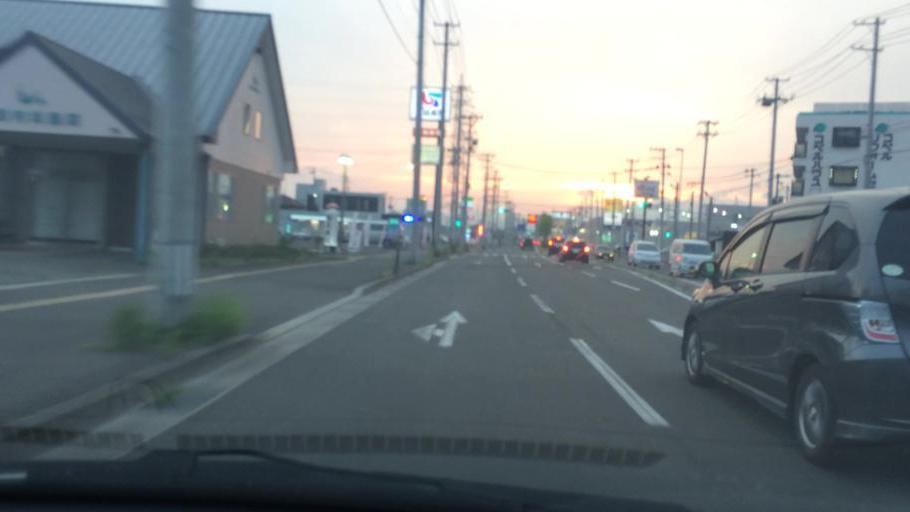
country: JP
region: Miyagi
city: Sendai-shi
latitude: 38.3126
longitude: 140.9116
